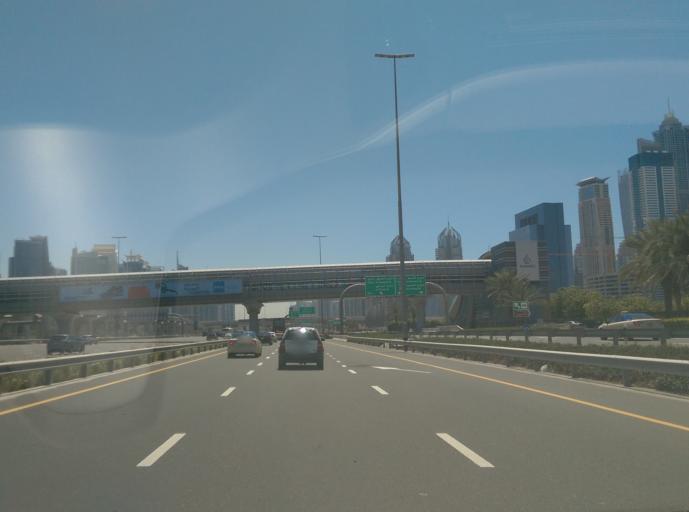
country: AE
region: Dubai
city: Dubai
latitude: 25.0902
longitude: 55.1582
